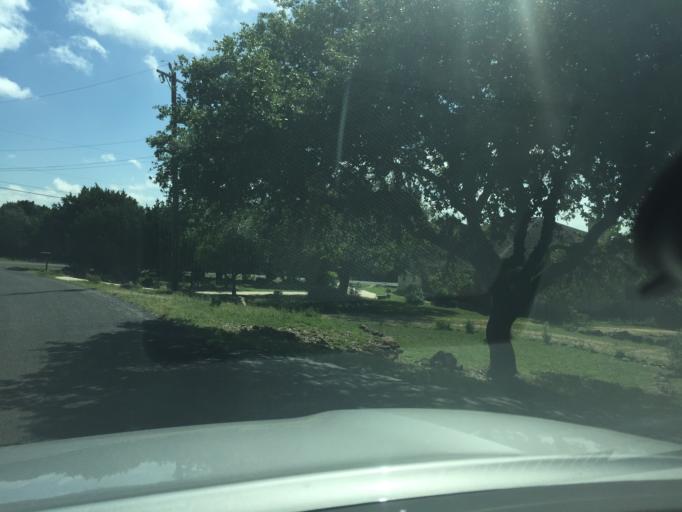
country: US
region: Texas
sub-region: Bexar County
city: Timberwood Park
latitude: 29.7021
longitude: -98.4875
